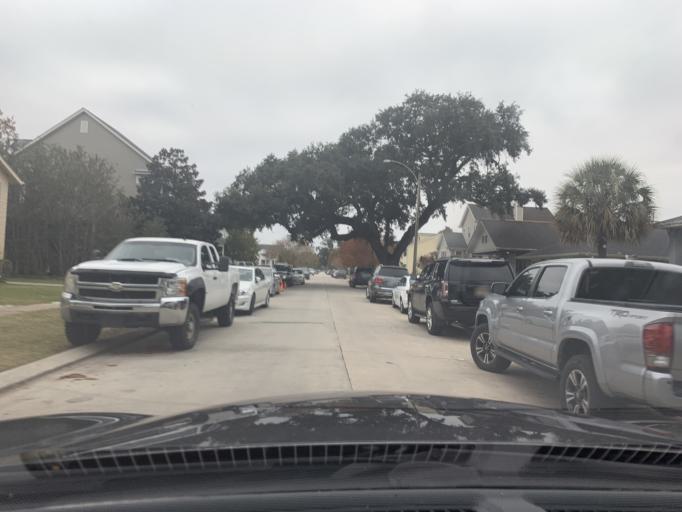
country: US
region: Louisiana
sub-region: Jefferson Parish
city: Metairie
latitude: 30.0046
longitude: -90.1114
